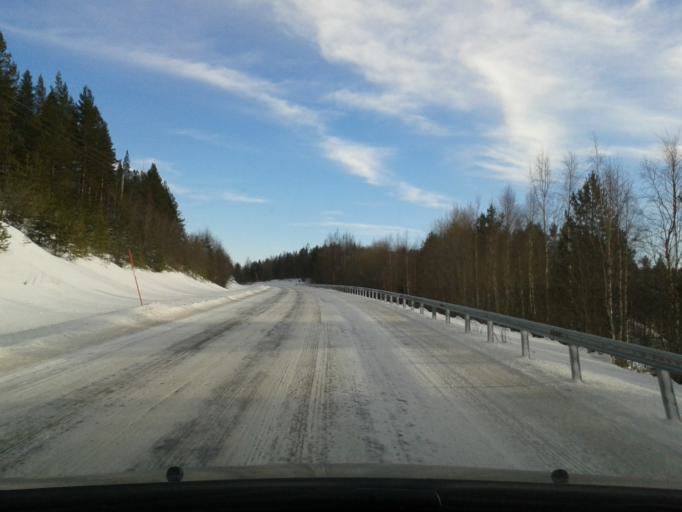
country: SE
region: Vaesterbotten
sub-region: Asele Kommun
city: Asele
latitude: 64.3246
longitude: 17.0691
